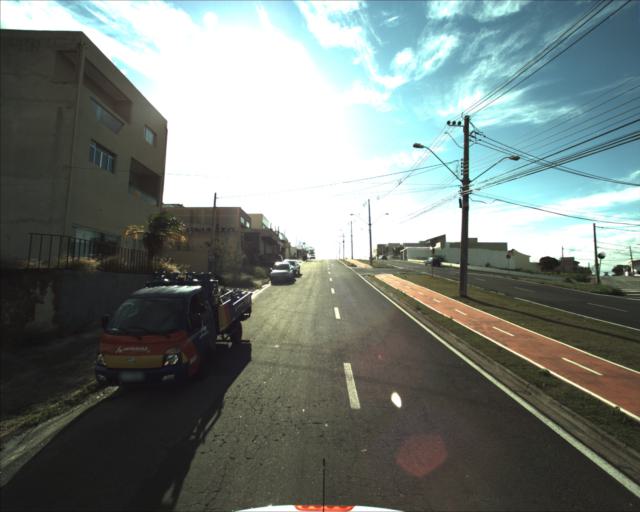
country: BR
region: Sao Paulo
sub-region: Sorocaba
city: Sorocaba
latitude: -23.5130
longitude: -47.5134
